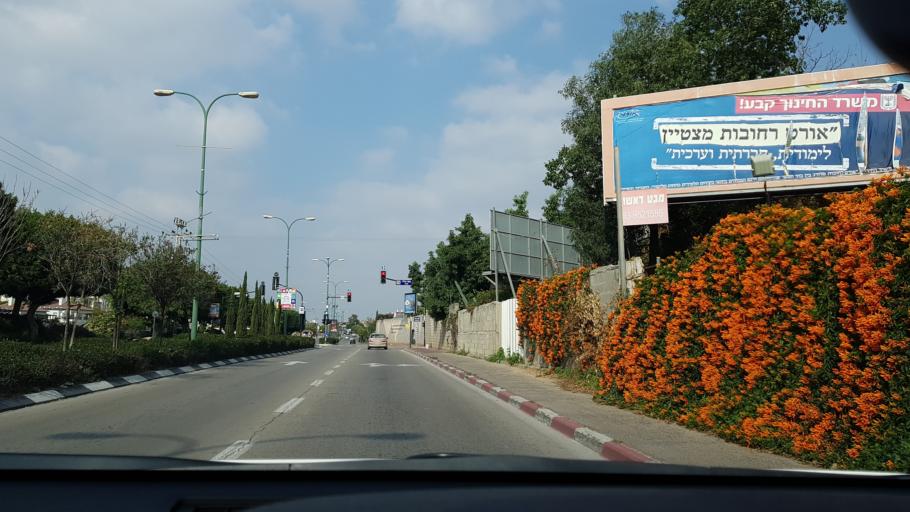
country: IL
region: Central District
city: Mazkeret Batya
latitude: 31.8769
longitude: 34.8188
